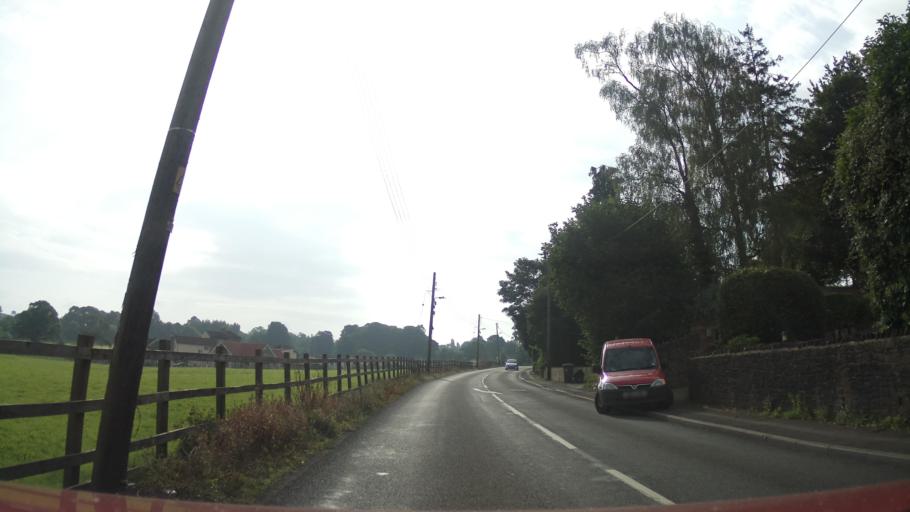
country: GB
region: England
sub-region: North Somerset
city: Long Ashton
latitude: 51.4256
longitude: -2.6991
